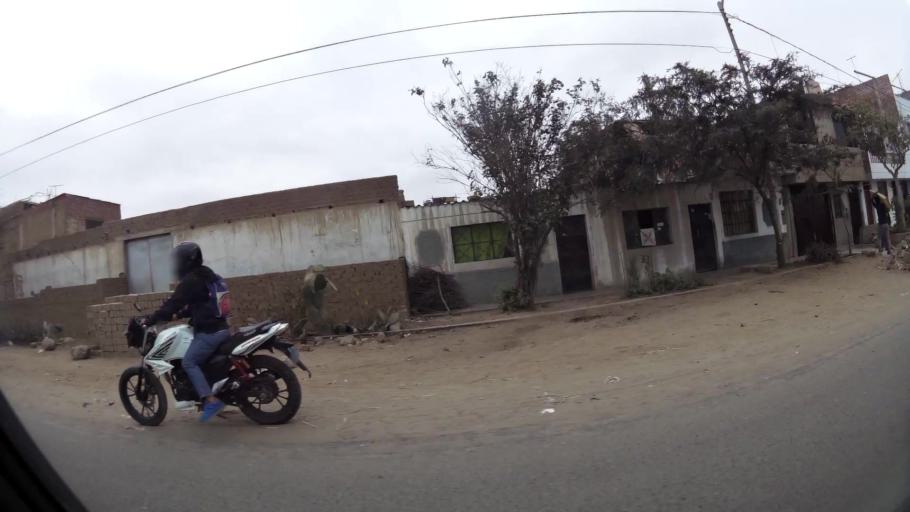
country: PE
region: La Libertad
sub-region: Provincia de Trujillo
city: La Esperanza
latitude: -8.0799
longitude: -79.0559
